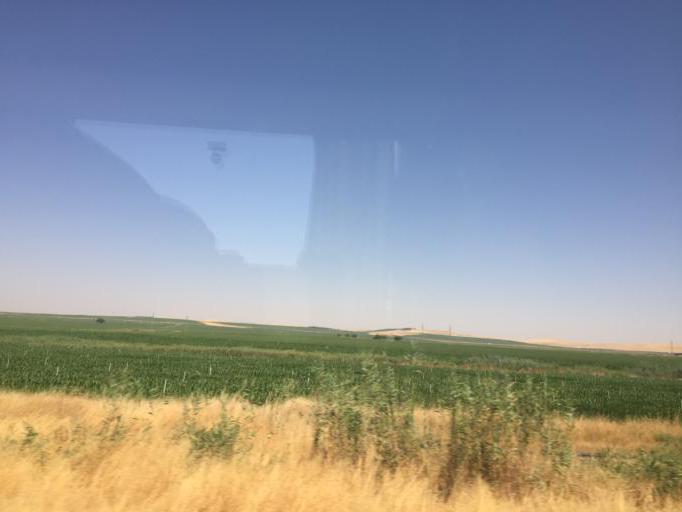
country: TR
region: Diyarbakir
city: Tepe
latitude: 37.8506
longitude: 40.7699
